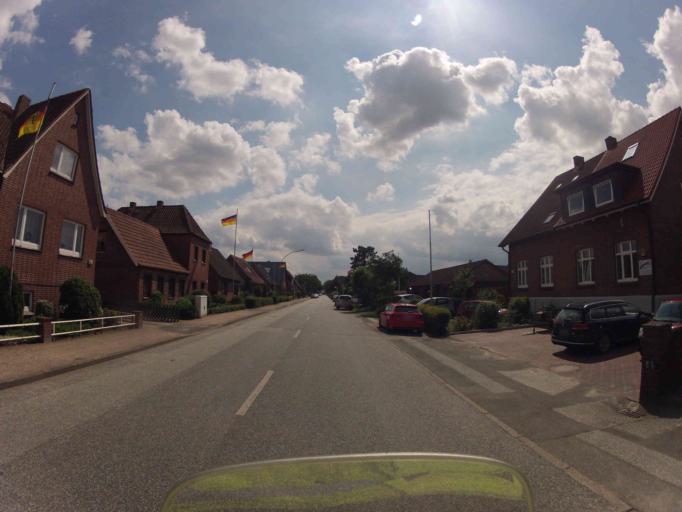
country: DE
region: Lower Saxony
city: Winsen
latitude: 53.4033
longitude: 10.1852
